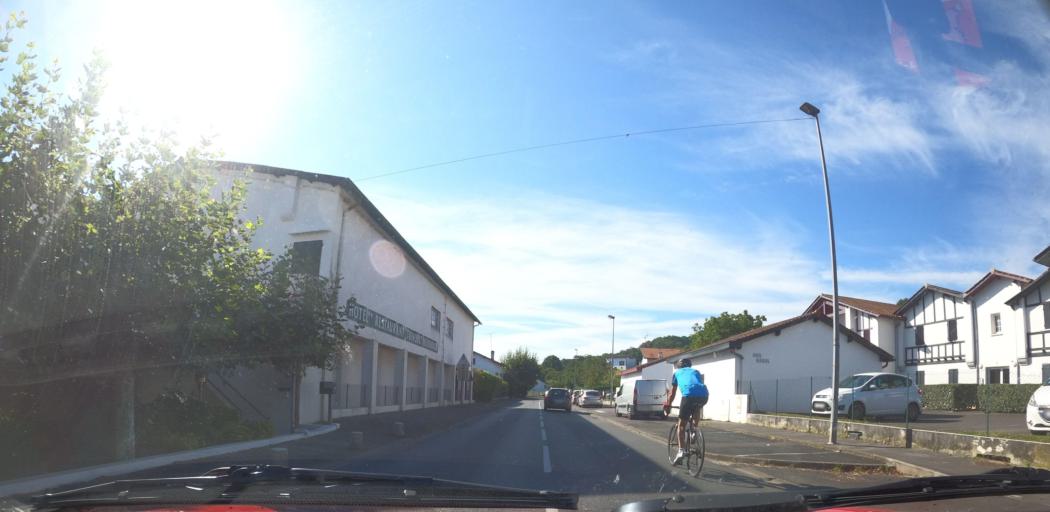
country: FR
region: Aquitaine
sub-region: Departement des Pyrenees-Atlantiques
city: Saint-Pee-sur-Nivelle
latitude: 43.3350
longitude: -1.5485
